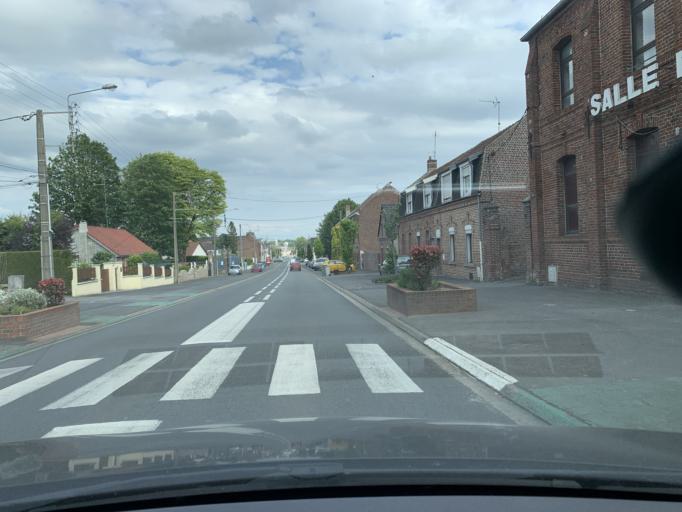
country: FR
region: Nord-Pas-de-Calais
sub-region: Departement du Nord
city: Proville
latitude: 50.1809
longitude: 3.2043
